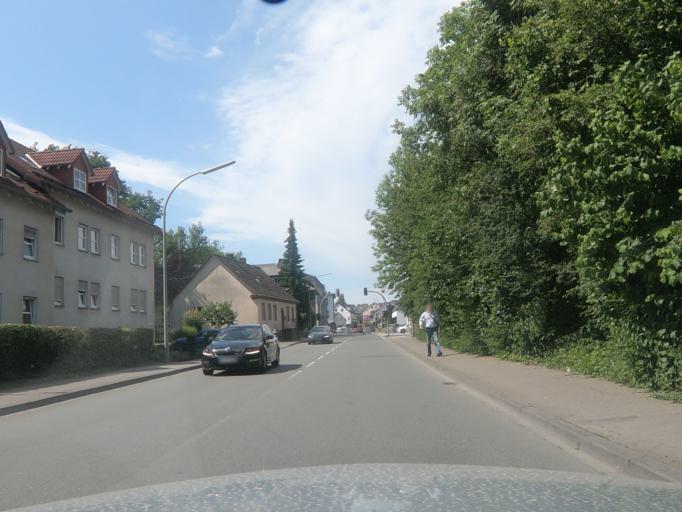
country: DE
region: North Rhine-Westphalia
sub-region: Regierungsbezirk Arnsberg
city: Sundern
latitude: 51.3169
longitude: 8.0088
